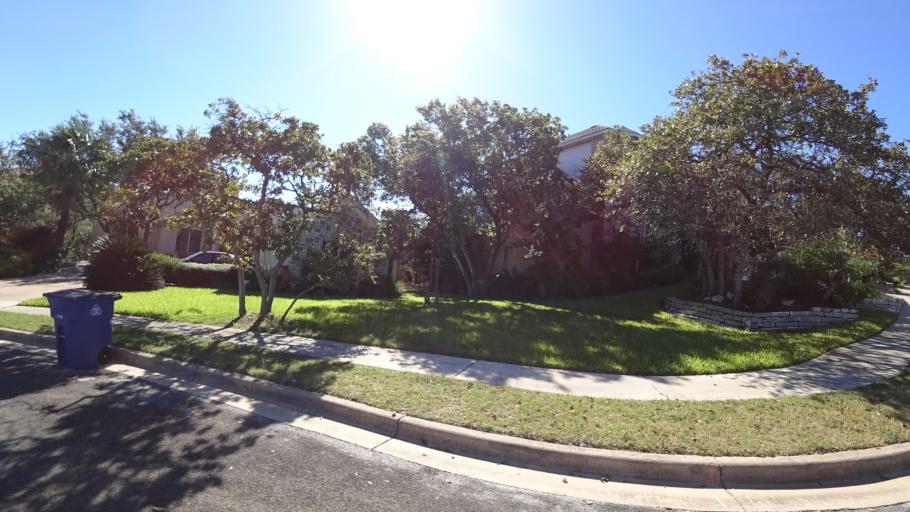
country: US
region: Texas
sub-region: Travis County
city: West Lake Hills
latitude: 30.3550
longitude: -97.7755
